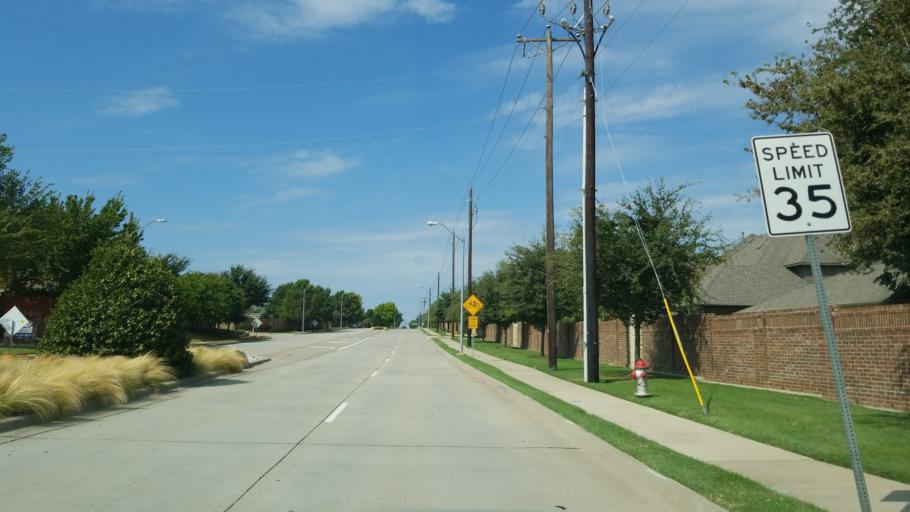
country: US
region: Texas
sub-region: Tarrant County
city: Euless
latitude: 32.8812
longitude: -97.0777
